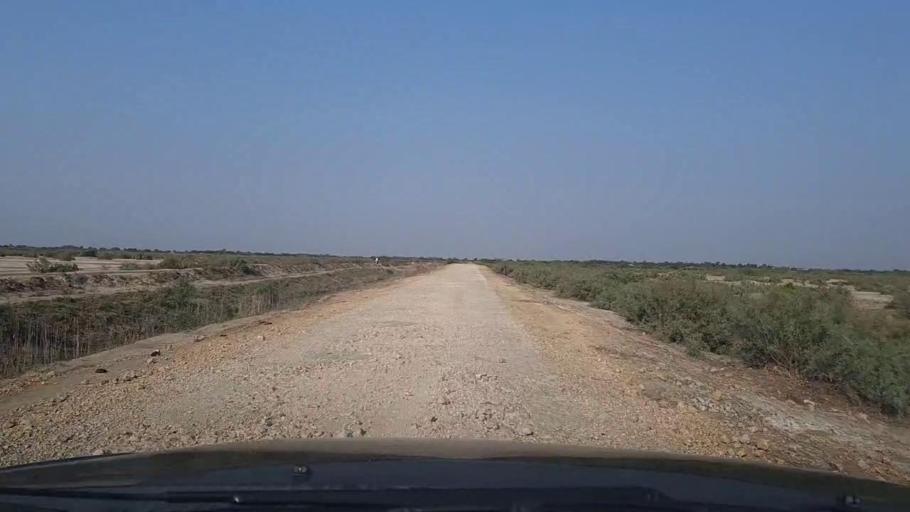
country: PK
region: Sindh
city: Mirpur Sakro
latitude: 24.6470
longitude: 67.7544
